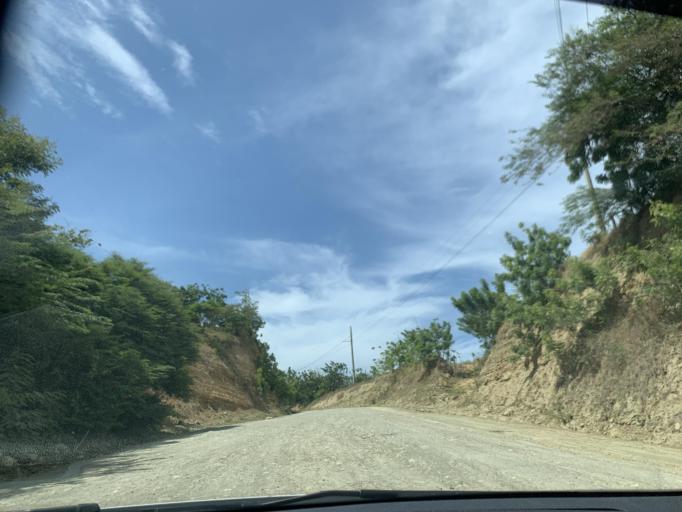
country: DO
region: Puerto Plata
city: Imbert
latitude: 19.8683
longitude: -70.8218
